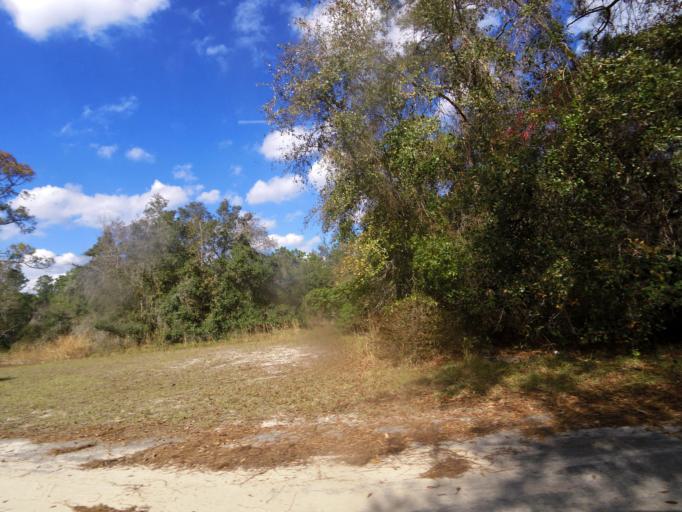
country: US
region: Florida
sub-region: Clay County
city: Middleburg
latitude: 30.1207
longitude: -81.9323
